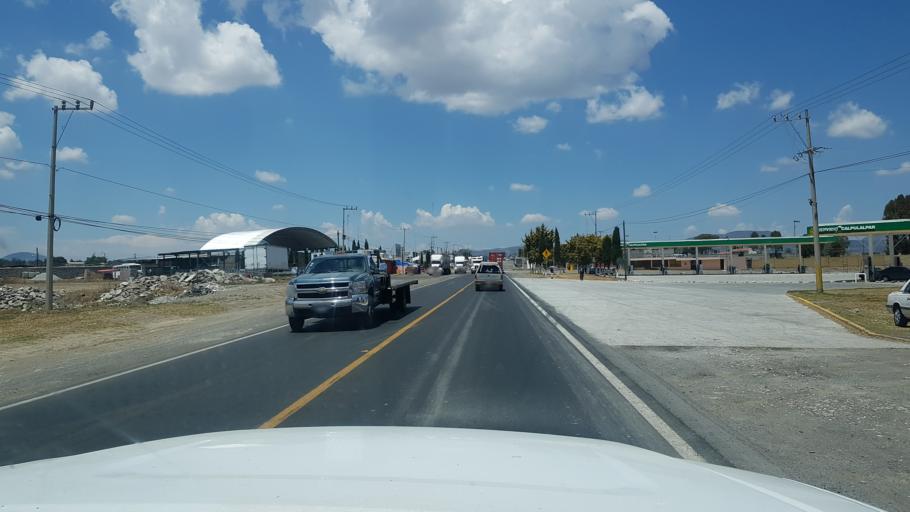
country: MX
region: Hidalgo
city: Calpulalpan
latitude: 19.5851
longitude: -98.5419
